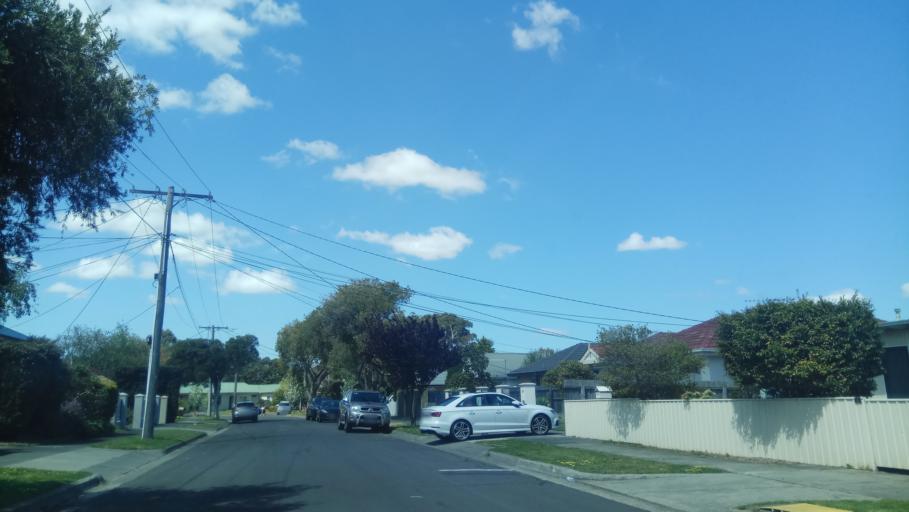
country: AU
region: Victoria
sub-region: Kingston
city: Dingley Village
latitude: -37.9828
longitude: 145.1342
